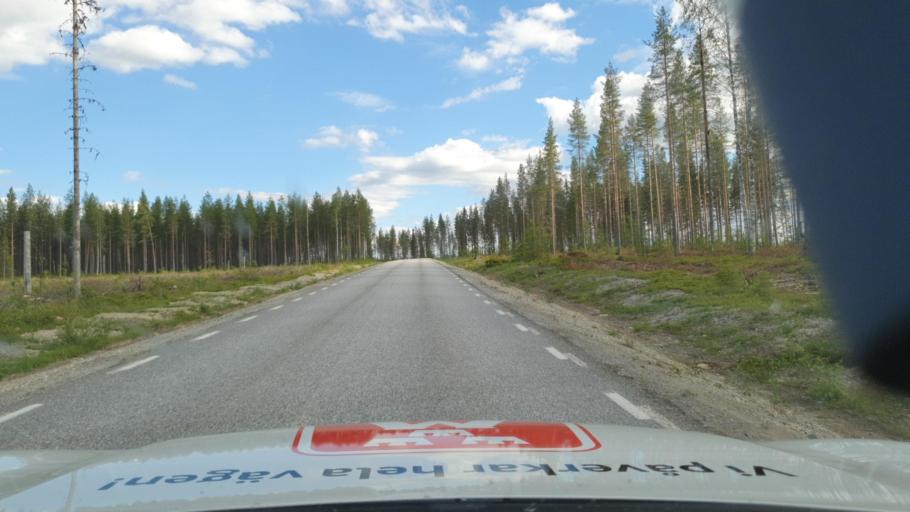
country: SE
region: Vaesterbotten
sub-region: Skelleftea Kommun
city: Langsele
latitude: 64.7020
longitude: 19.9932
